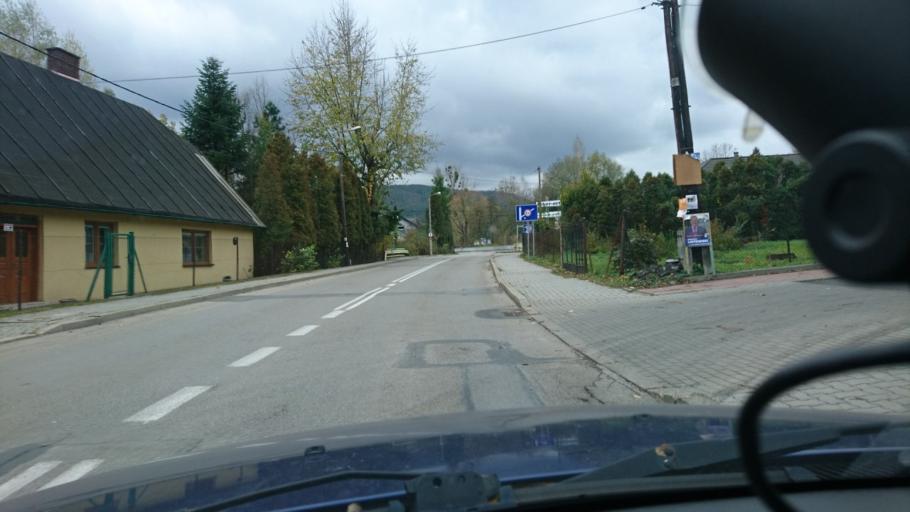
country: PL
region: Silesian Voivodeship
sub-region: Bielsko-Biala
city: Bielsko-Biala
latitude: 49.7985
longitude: 19.0165
